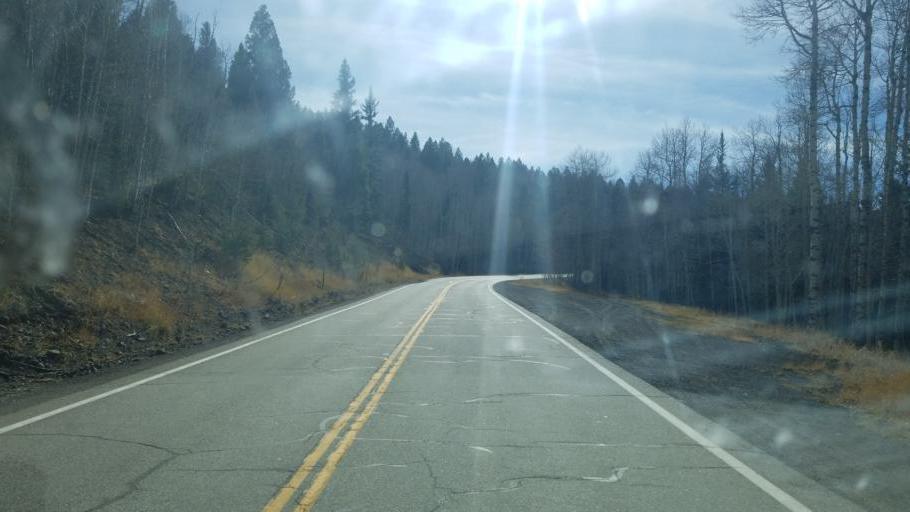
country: US
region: New Mexico
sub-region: Rio Arriba County
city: Chama
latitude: 37.1217
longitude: -106.3639
